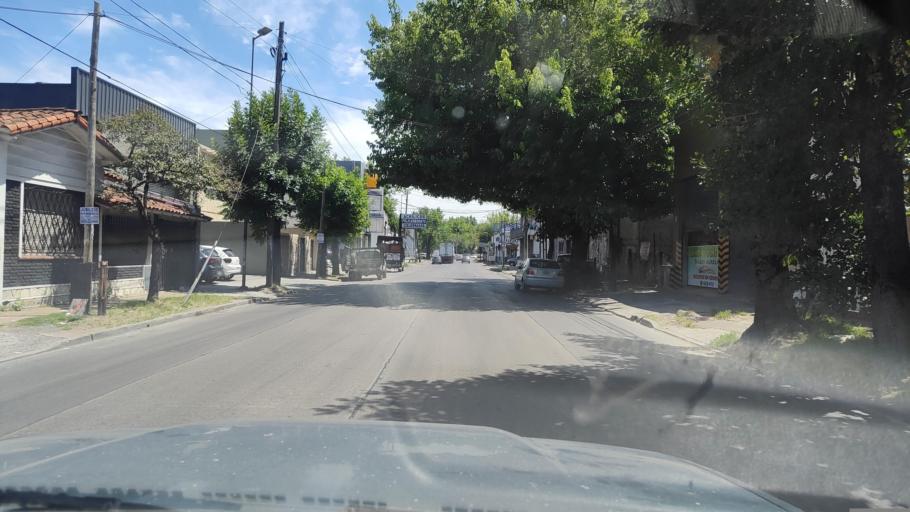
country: AR
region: Buenos Aires
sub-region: Partido de Moron
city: Moron
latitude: -34.6545
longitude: -58.6299
